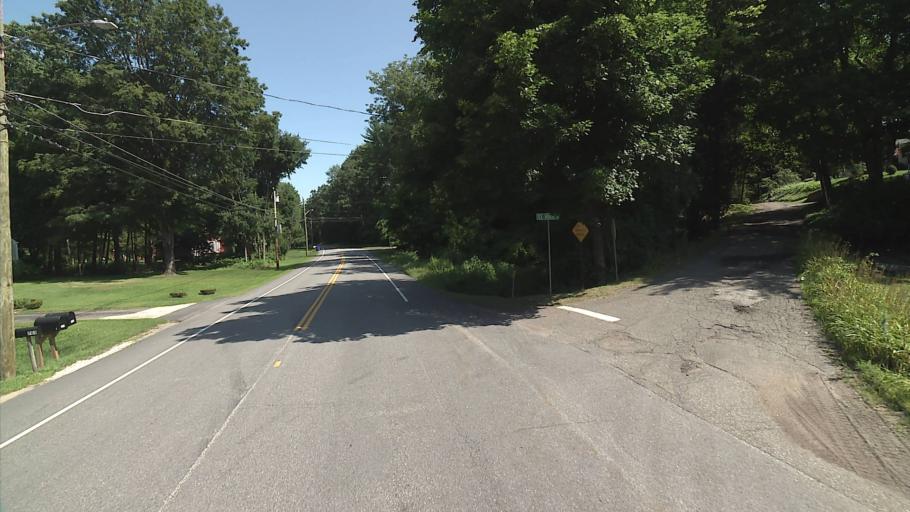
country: US
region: Connecticut
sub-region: Litchfield County
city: West Torrington
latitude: 41.8320
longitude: -73.1513
